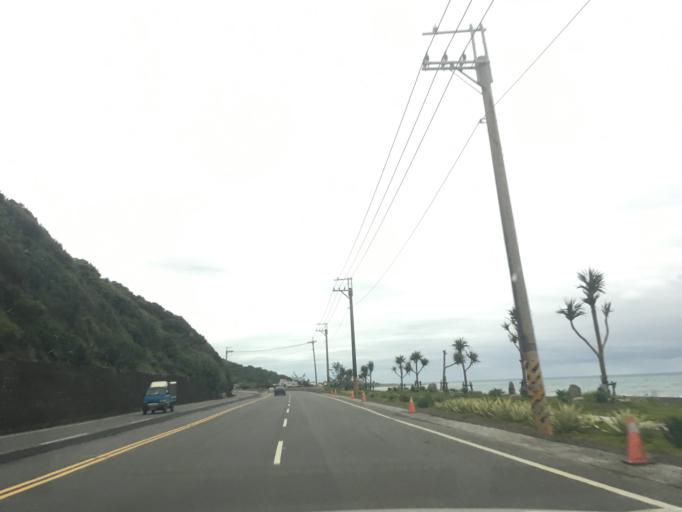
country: TW
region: Taiwan
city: Hengchun
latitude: 22.3469
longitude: 120.8995
